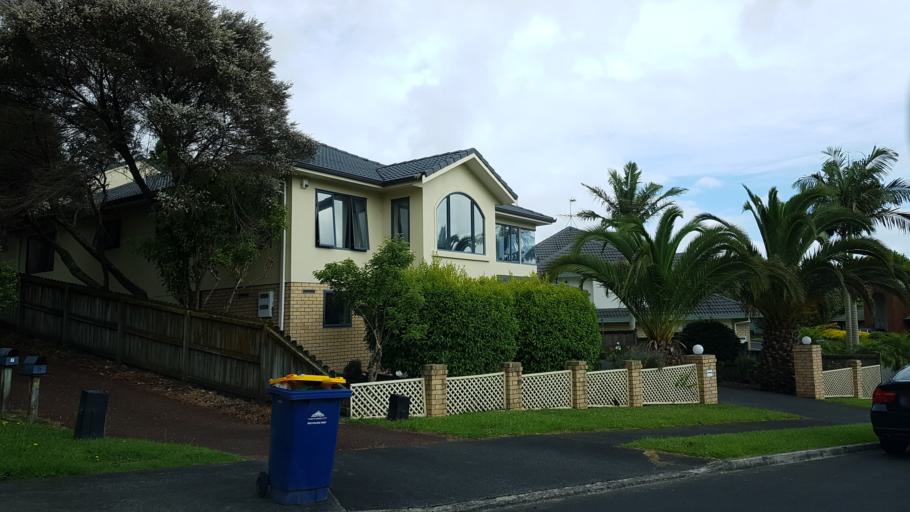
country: NZ
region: Auckland
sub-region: Auckland
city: North Shore
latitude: -36.7879
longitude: 174.7342
